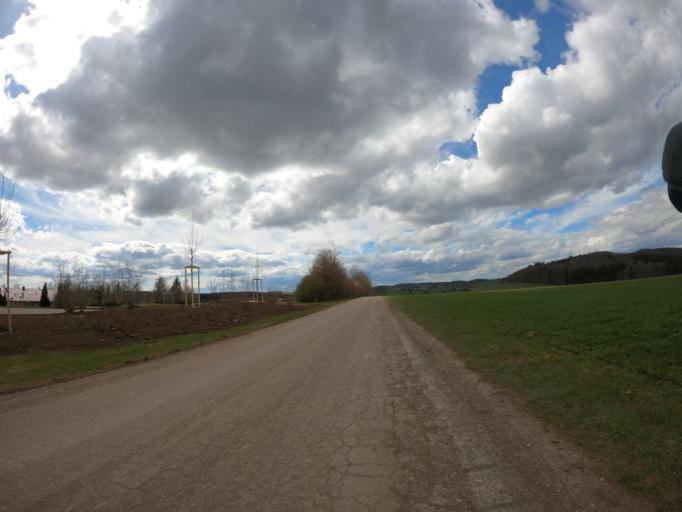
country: DE
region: Baden-Wuerttemberg
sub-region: Tuebingen Region
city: Pfullingen
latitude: 48.3881
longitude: 9.2189
